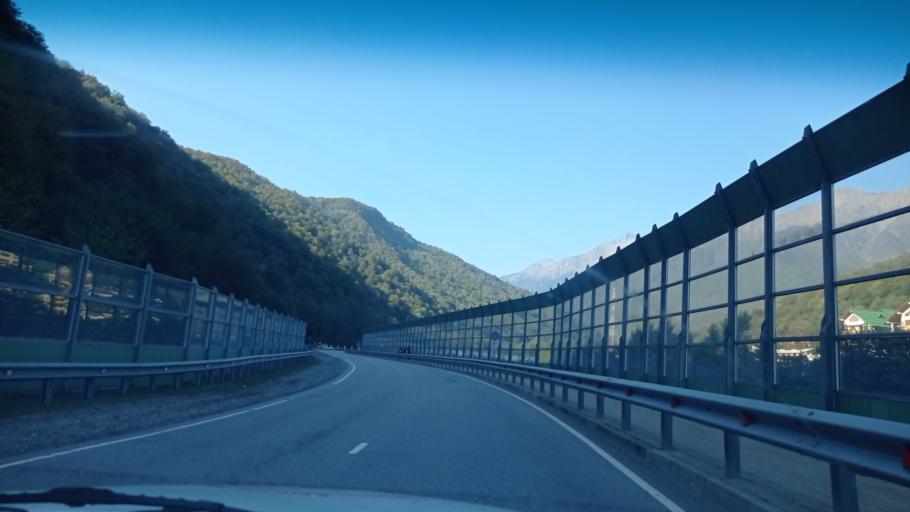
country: RU
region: Krasnodarskiy
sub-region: Sochi City
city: Krasnaya Polyana
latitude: 43.6899
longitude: 40.2737
